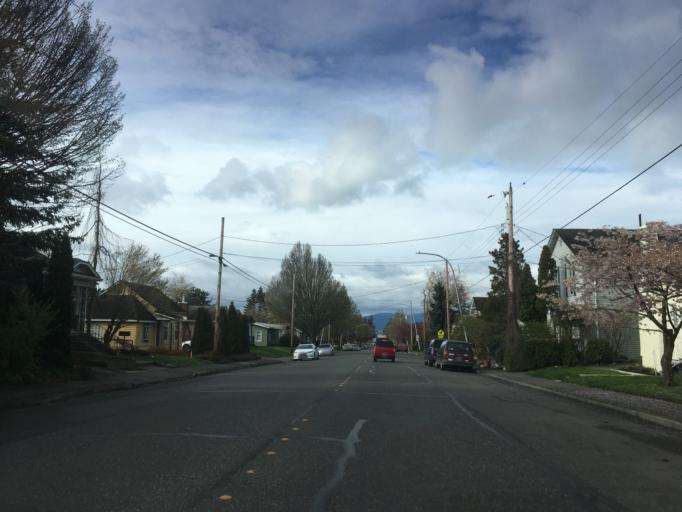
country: US
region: Washington
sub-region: Whatcom County
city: Bellingham
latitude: 48.7614
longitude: -122.4784
